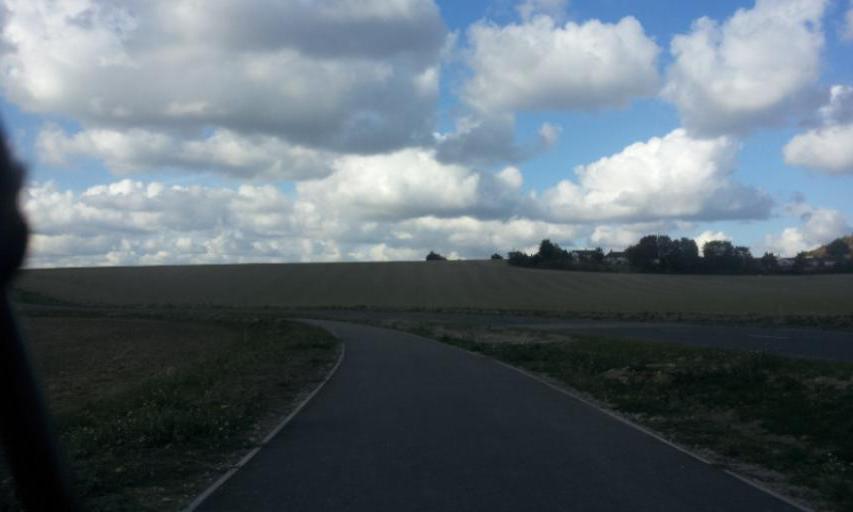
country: GB
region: England
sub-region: Kent
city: Aylesford
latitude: 51.3281
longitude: 0.4791
